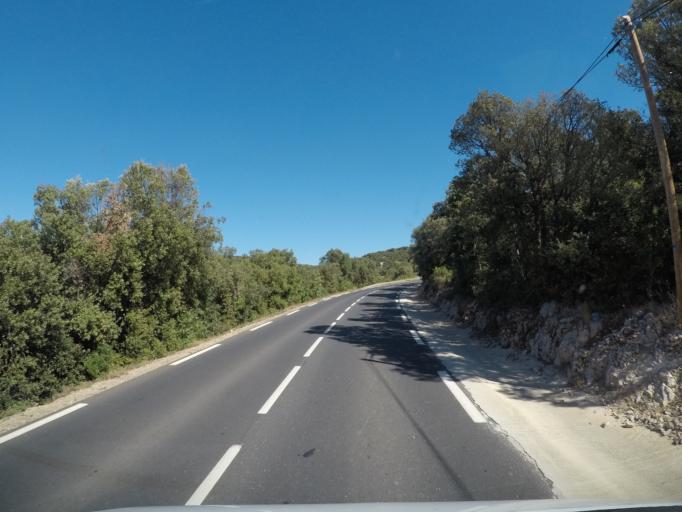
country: FR
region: Languedoc-Roussillon
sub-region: Departement de l'Herault
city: Aniane
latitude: 43.7209
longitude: 3.6248
